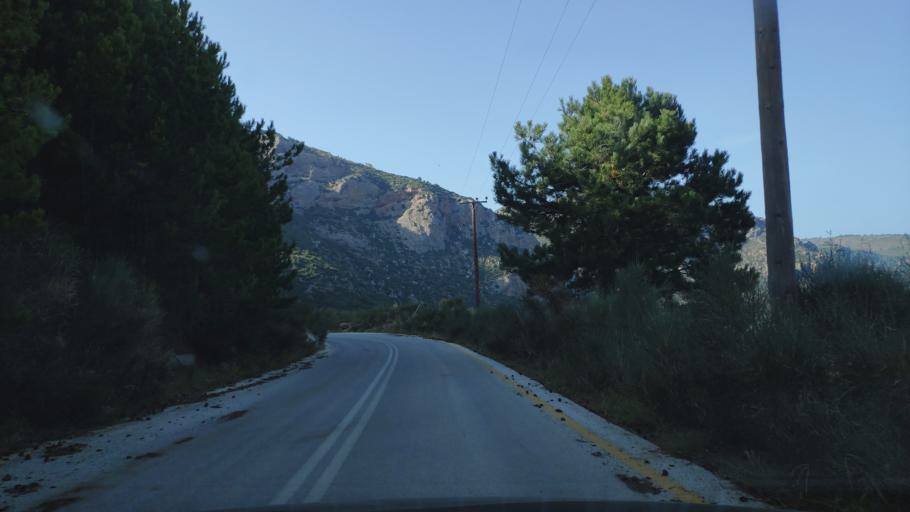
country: GR
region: West Greece
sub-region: Nomos Achaias
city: Aiyira
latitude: 38.0588
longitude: 22.3810
